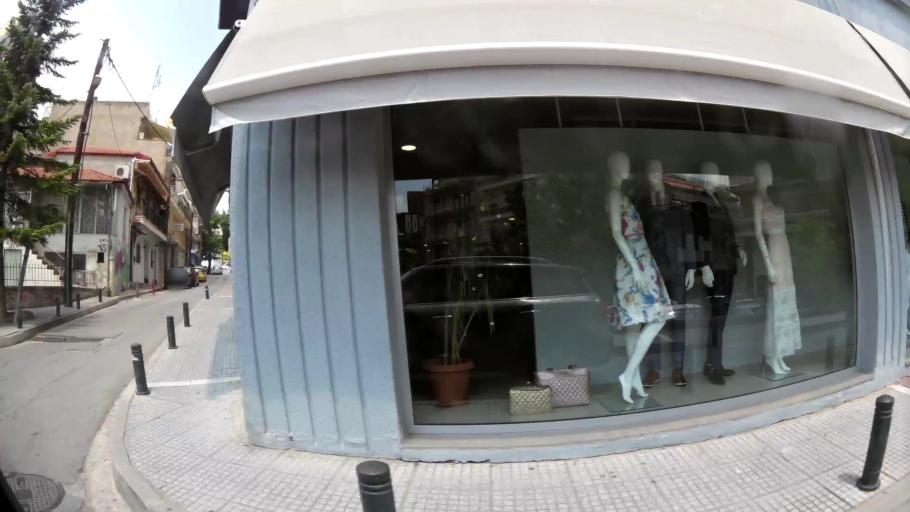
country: GR
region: West Macedonia
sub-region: Nomos Kozanis
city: Kozani
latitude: 40.3012
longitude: 21.7909
